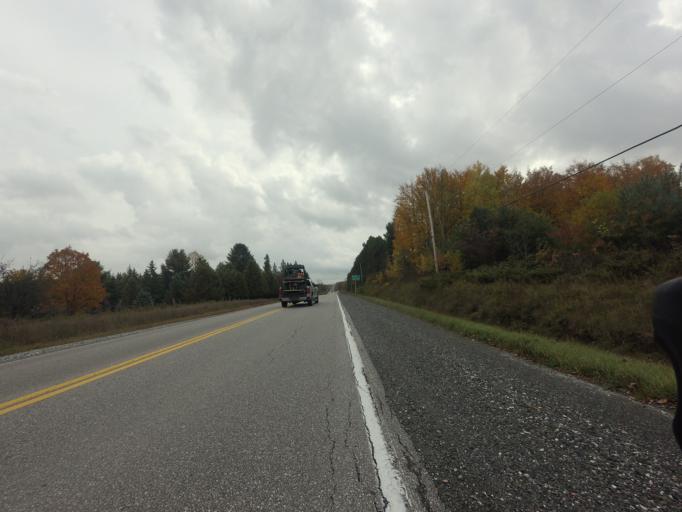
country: CA
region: Ontario
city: Perth
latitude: 45.0966
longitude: -76.4640
